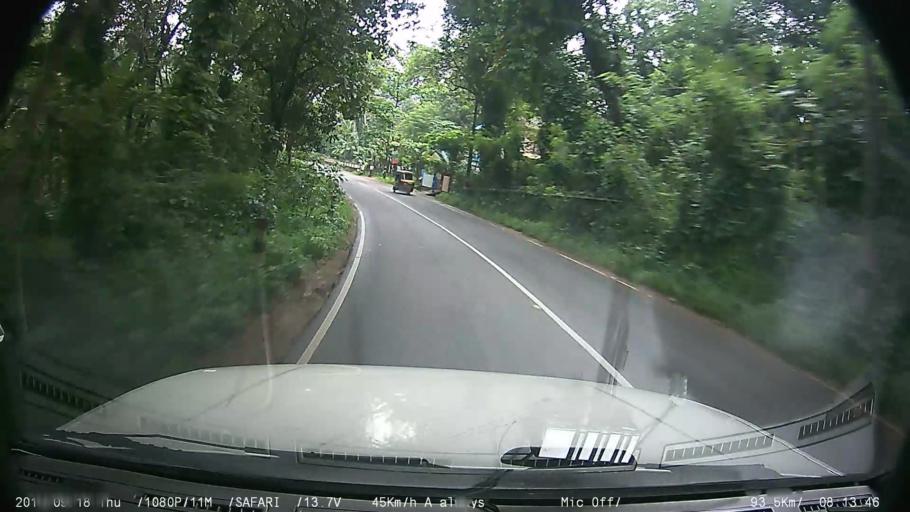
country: IN
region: Kerala
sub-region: Kottayam
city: Kottayam
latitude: 9.6171
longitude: 76.6045
